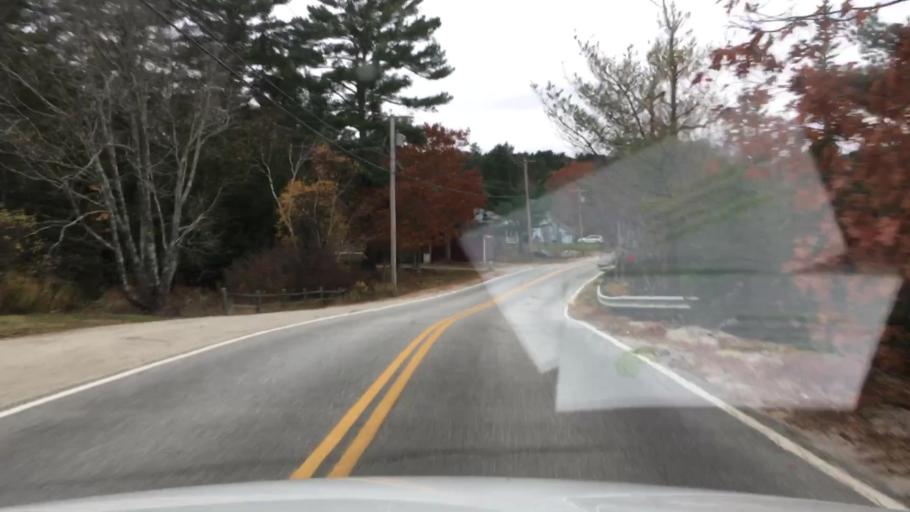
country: US
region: Maine
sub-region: Hancock County
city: Sedgwick
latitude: 44.3784
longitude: -68.5639
